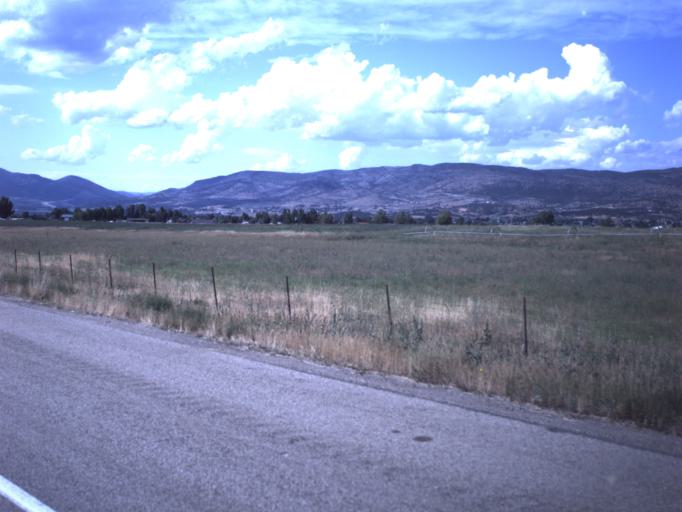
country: US
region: Utah
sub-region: Wasatch County
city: Heber
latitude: 40.4652
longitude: -111.3849
